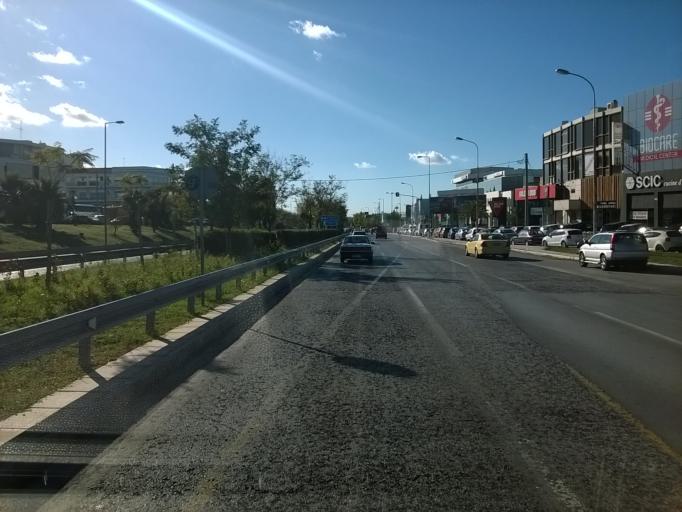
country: GR
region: Attica
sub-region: Nomarchia Athinas
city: Argyroupoli
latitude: 37.9176
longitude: 23.7443
